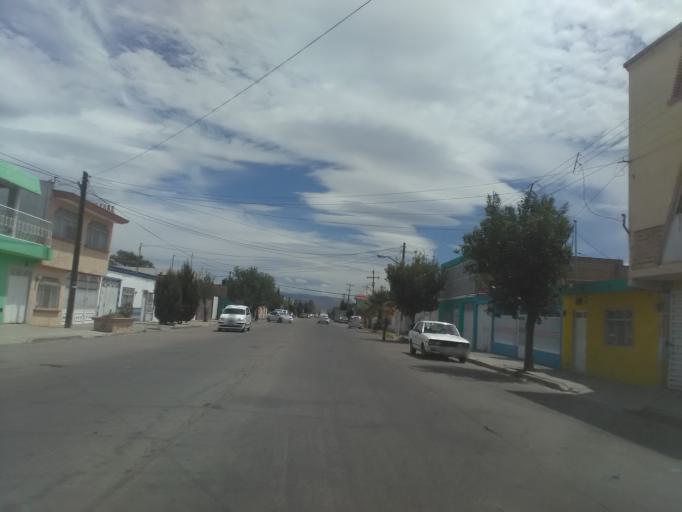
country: MX
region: Durango
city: Victoria de Durango
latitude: 24.0238
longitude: -104.6312
